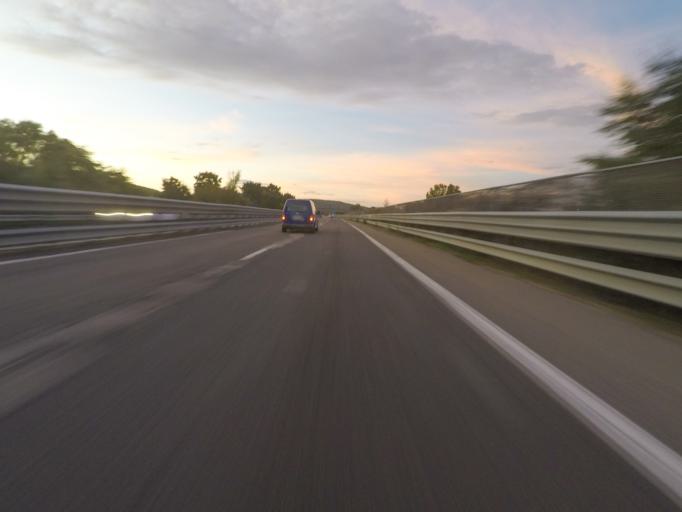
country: IT
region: Tuscany
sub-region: Province of Arezzo
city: Lucignano
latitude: 43.2446
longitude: 11.7216
